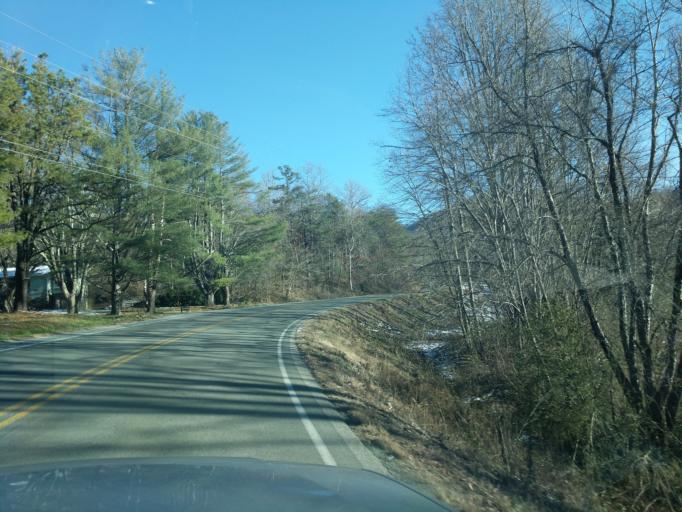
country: US
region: Georgia
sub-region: Towns County
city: Hiawassee
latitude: 34.9310
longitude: -83.6616
